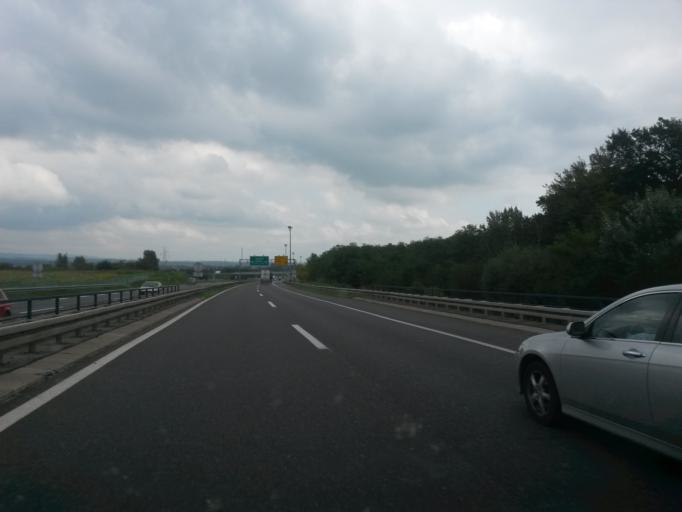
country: HR
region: Grad Zagreb
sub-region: Sesvete
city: Sesvete
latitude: 45.8472
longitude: 16.1452
